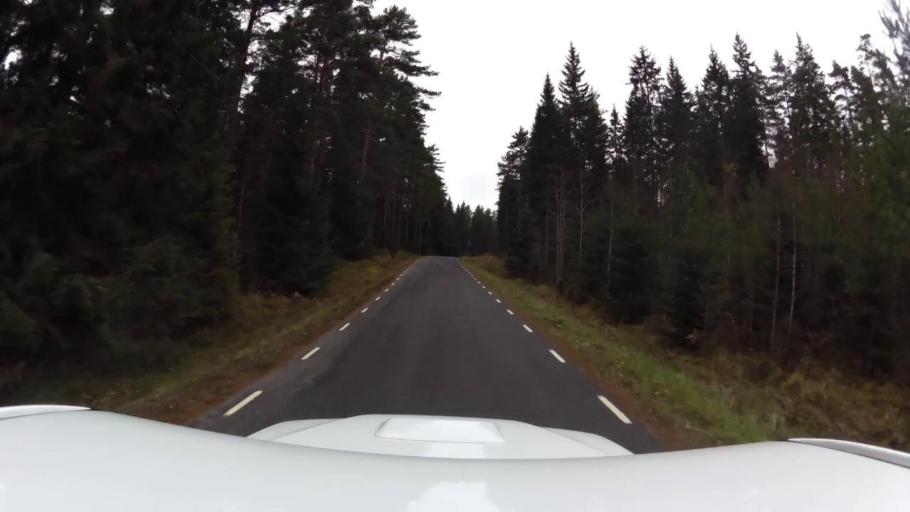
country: SE
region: OEstergoetland
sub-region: Kinda Kommun
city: Rimforsa
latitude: 58.1374
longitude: 15.4529
